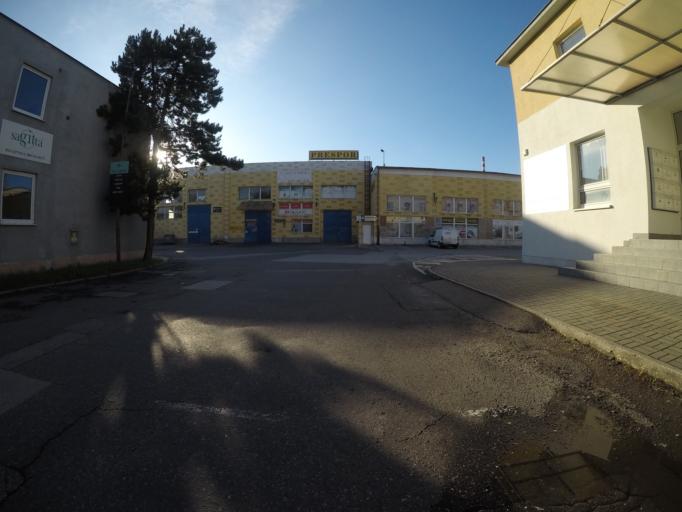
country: SK
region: Bratislavsky
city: Bratislava
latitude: 48.1733
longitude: 17.1559
